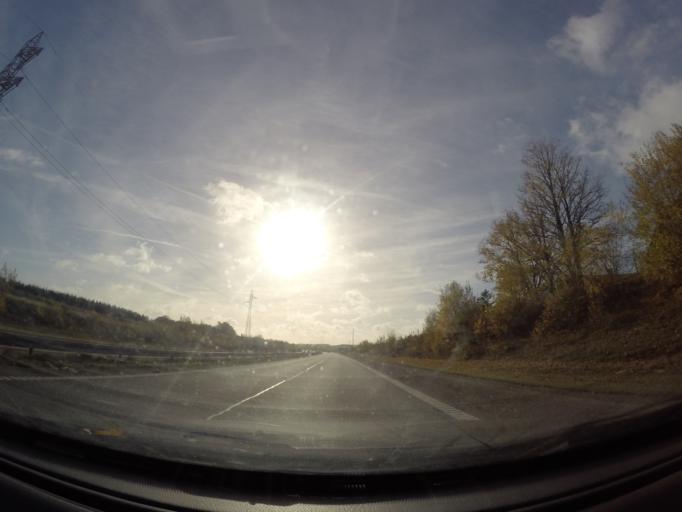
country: DK
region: South Denmark
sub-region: Svendborg Kommune
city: Svendborg
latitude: 55.1208
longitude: 10.5603
